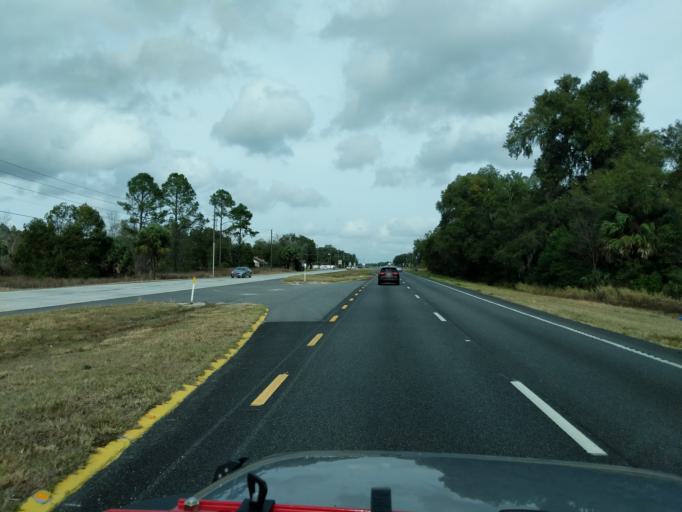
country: US
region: Florida
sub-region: Orange County
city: Tangerine
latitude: 28.7665
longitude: -81.6245
